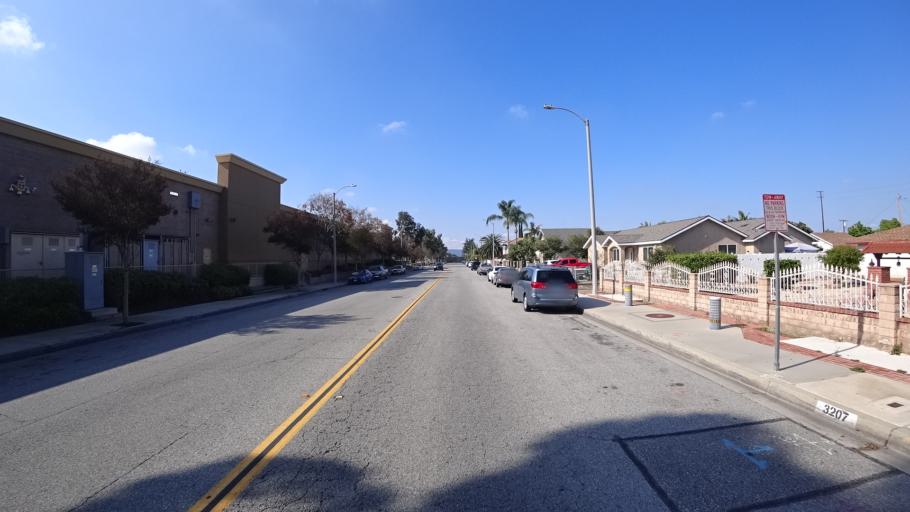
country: US
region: California
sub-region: Los Angeles County
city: Baldwin Park
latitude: 34.0723
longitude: -117.9641
